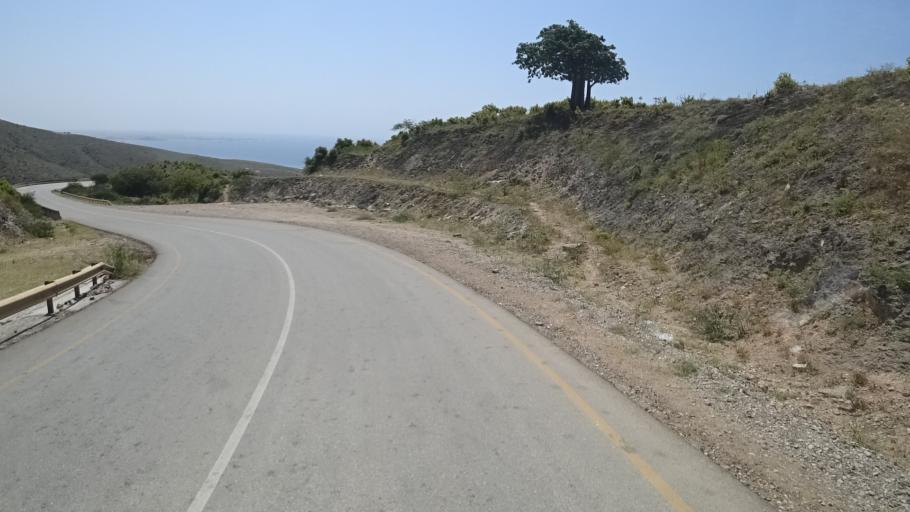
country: OM
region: Zufar
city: Salalah
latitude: 17.0505
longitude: 54.6108
